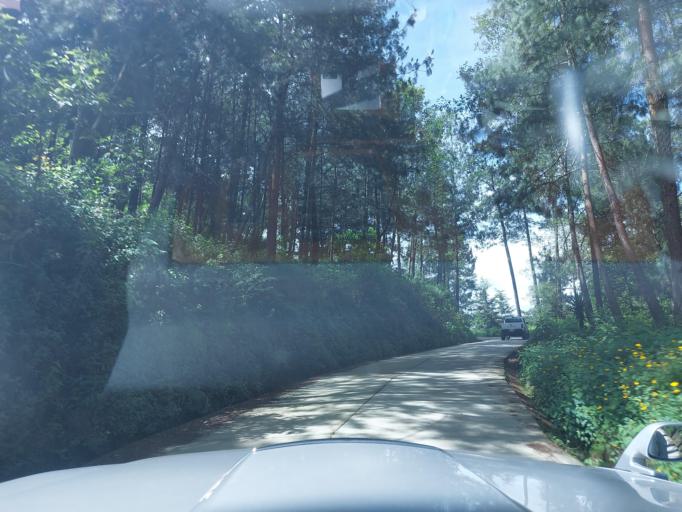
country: GT
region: Chimaltenango
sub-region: Municipio de San Juan Comalapa
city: Comalapa
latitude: 14.7526
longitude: -90.8671
